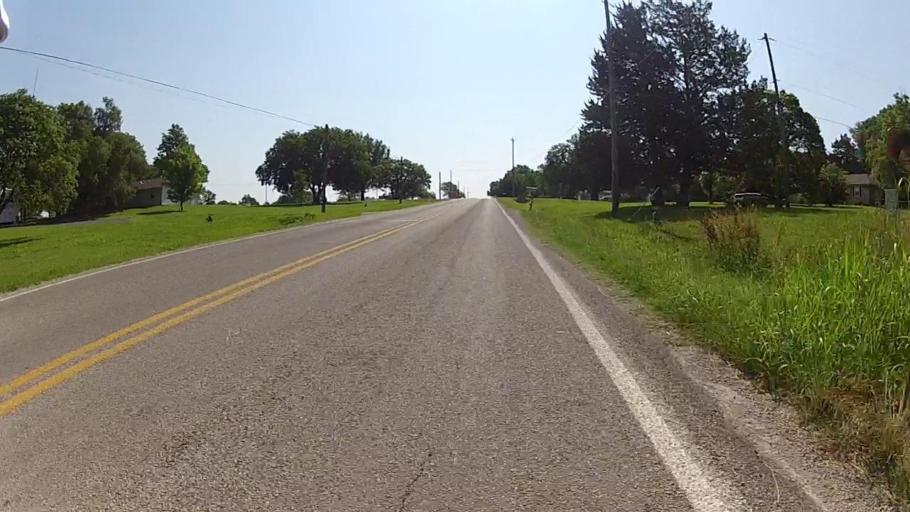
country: US
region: Kansas
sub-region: Montgomery County
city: Independence
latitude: 37.1929
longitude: -95.7242
